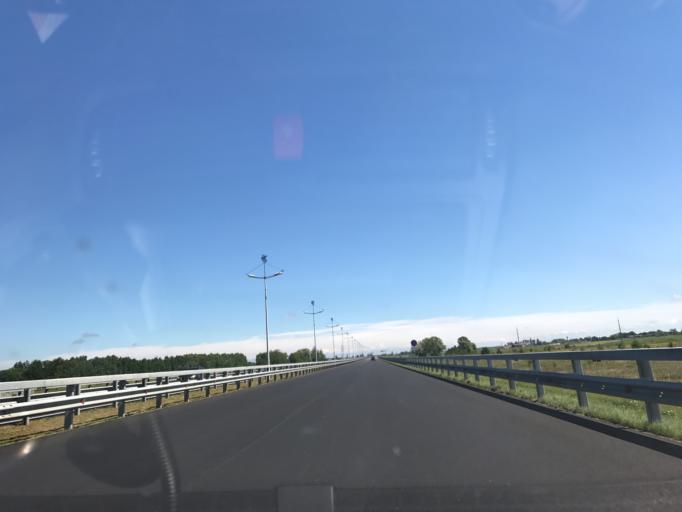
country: RU
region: Kaliningrad
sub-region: Zelenogradskiy Rayon
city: Zelenogradsk
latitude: 54.9192
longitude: 20.4400
